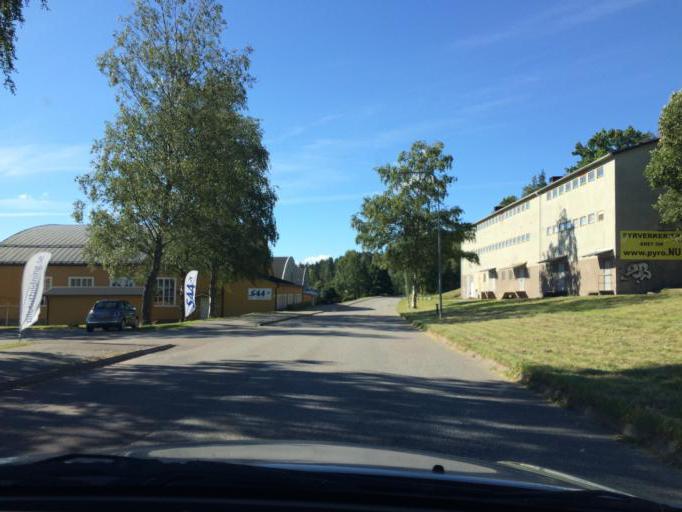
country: SE
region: Vaestmanland
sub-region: Vasteras
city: Vasteras
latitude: 59.5880
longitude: 16.6249
